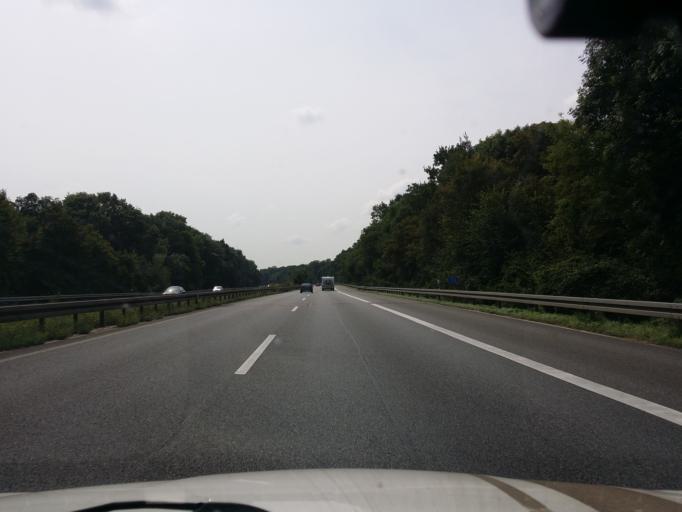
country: DE
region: Hesse
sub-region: Regierungsbezirk Darmstadt
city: Nauheim
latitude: 49.9479
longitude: 8.4776
